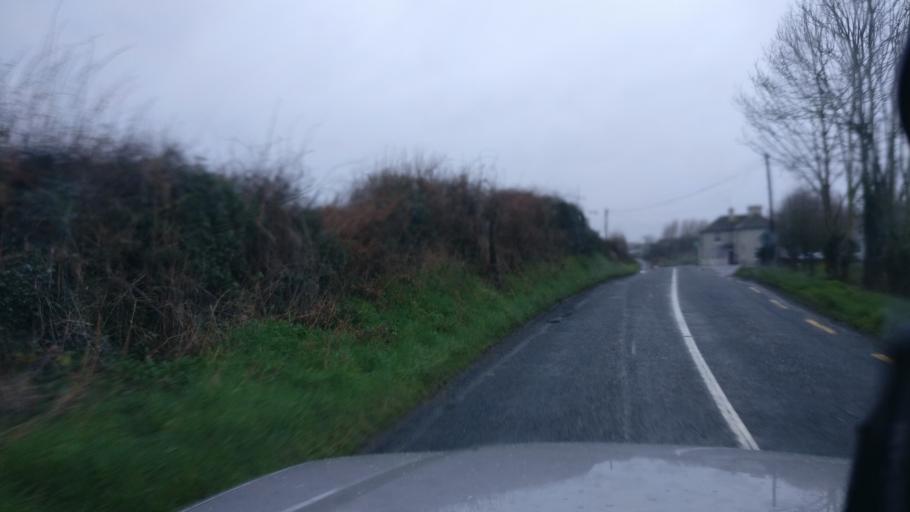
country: IE
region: Connaught
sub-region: County Galway
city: Loughrea
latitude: 53.1140
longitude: -8.4397
